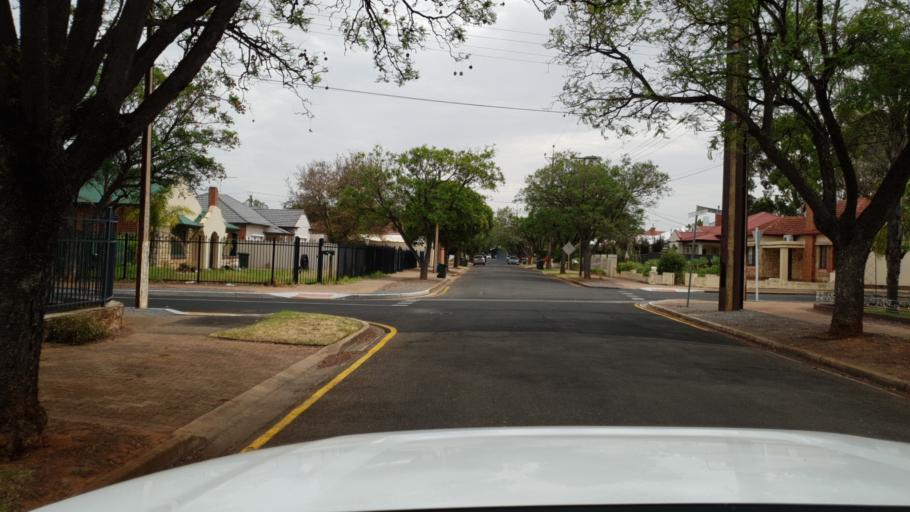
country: AU
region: South Australia
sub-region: Mitcham
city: Clarence Gardens
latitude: -34.9698
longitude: 138.5765
